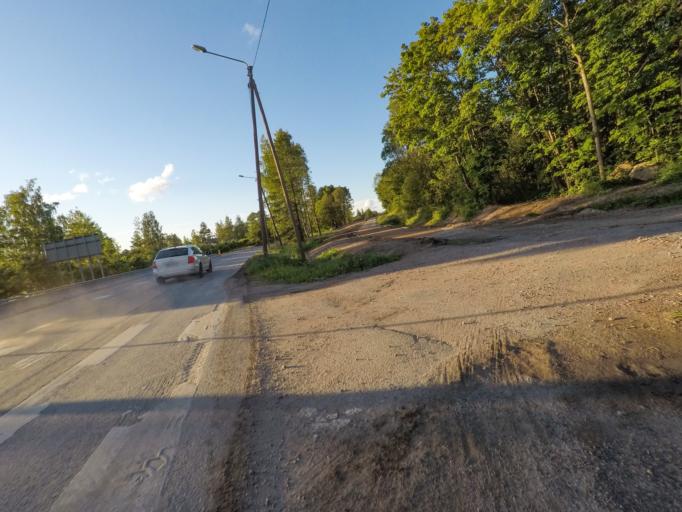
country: FI
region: South Karelia
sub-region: Imatra
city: Imatra
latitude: 61.1989
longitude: 28.7836
